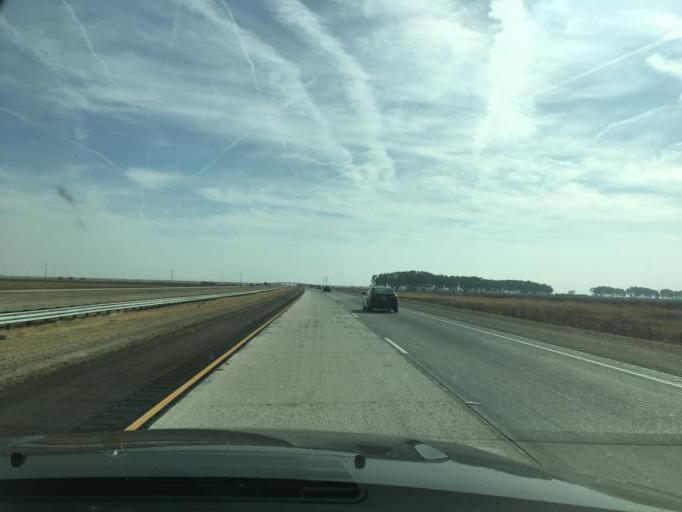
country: US
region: California
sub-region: Kern County
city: Lost Hills
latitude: 35.5715
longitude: -119.6128
